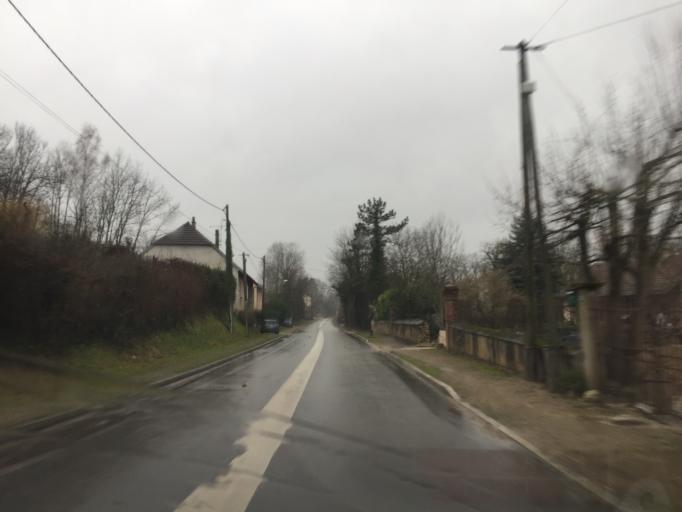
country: FR
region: Franche-Comte
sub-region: Departement du Doubs
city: Arc-et-Senans
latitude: 46.9982
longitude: 5.7581
